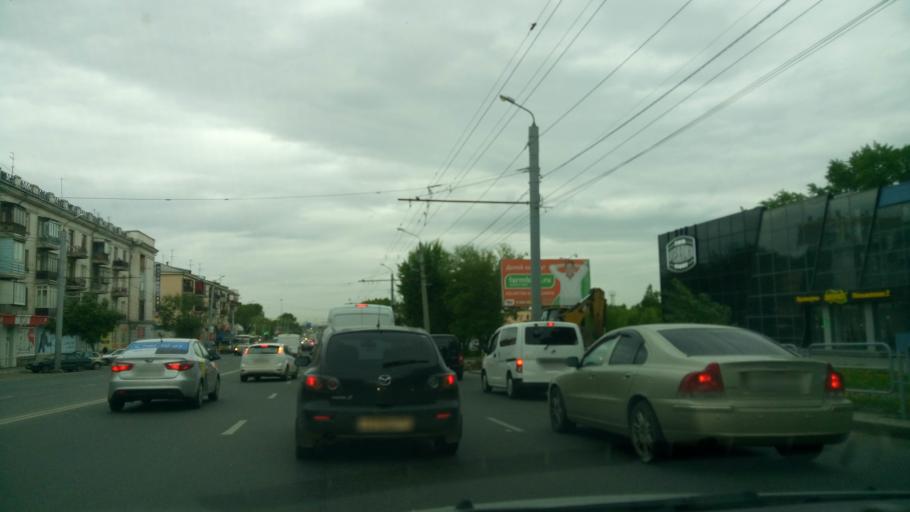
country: RU
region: Chelyabinsk
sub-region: Gorod Chelyabinsk
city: Chelyabinsk
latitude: 55.1898
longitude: 61.3865
